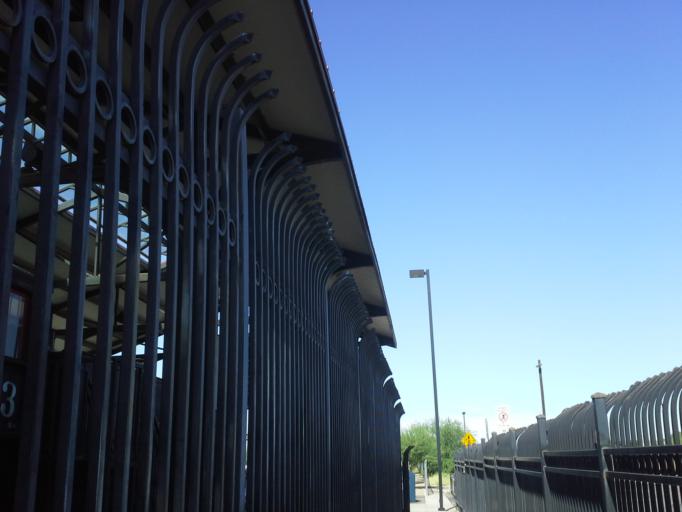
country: US
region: Arizona
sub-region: Pima County
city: South Tucson
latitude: 32.2239
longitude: -110.9673
